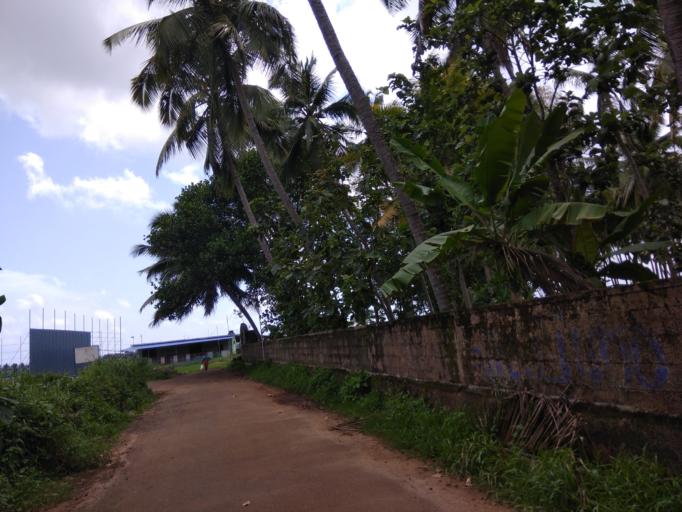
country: IN
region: Kerala
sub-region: Thrissur District
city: Trichur
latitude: 10.5373
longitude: 76.1399
